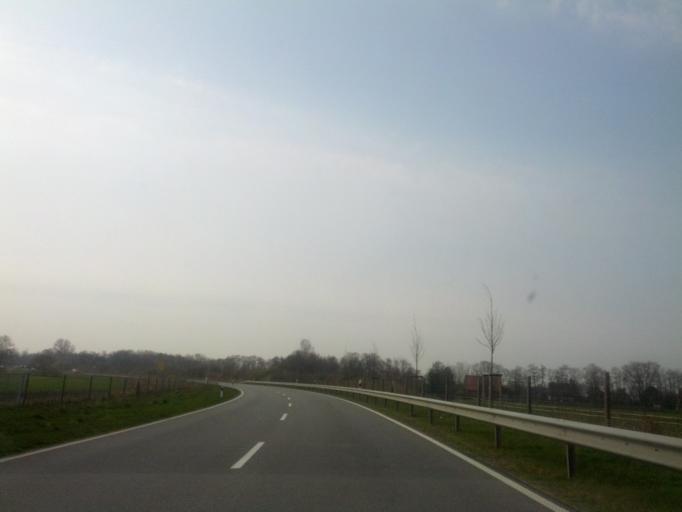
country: DE
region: Lower Saxony
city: Lutetsburg
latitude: 53.5877
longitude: 7.2303
